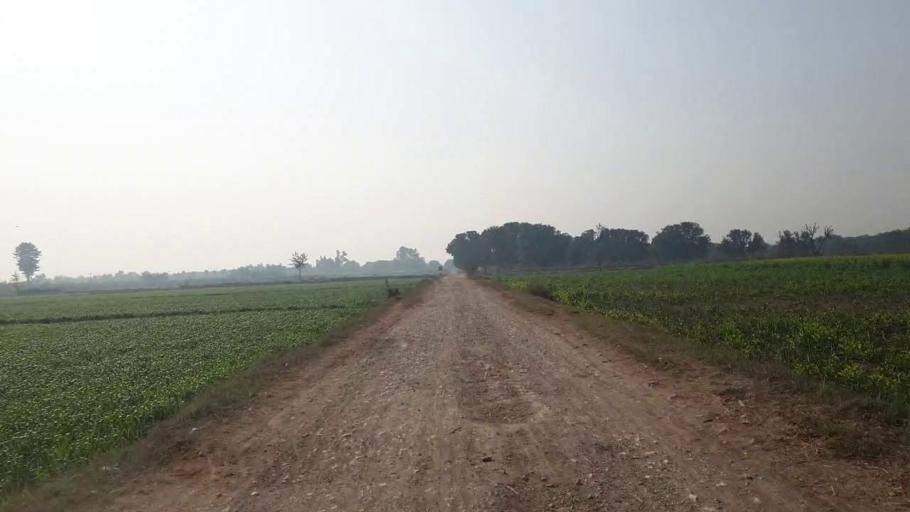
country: PK
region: Sindh
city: Sakrand
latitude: 25.9961
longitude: 68.3674
